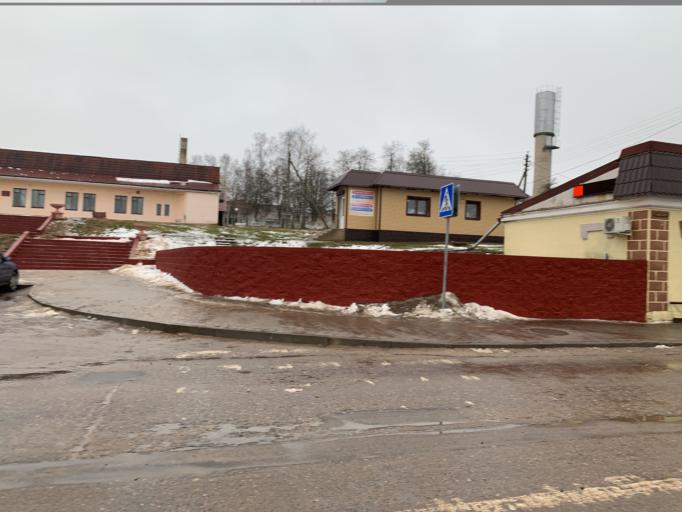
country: BY
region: Minsk
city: Haradzyeya
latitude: 53.3145
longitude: 26.5388
